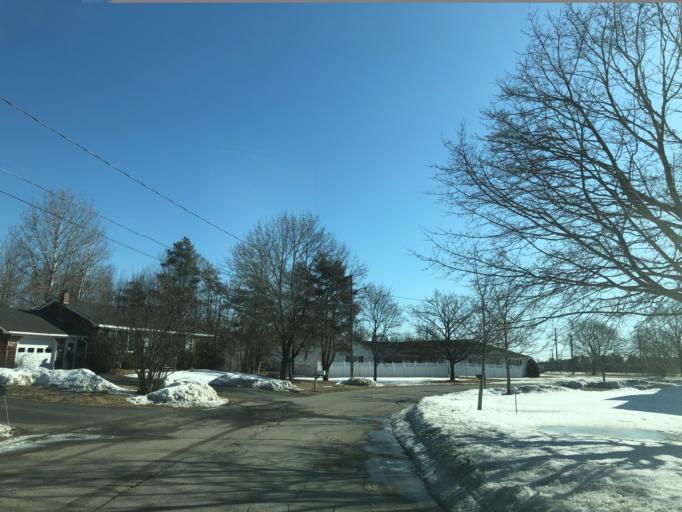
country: US
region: Maine
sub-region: Penobscot County
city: Brewer
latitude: 44.8209
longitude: -68.7468
